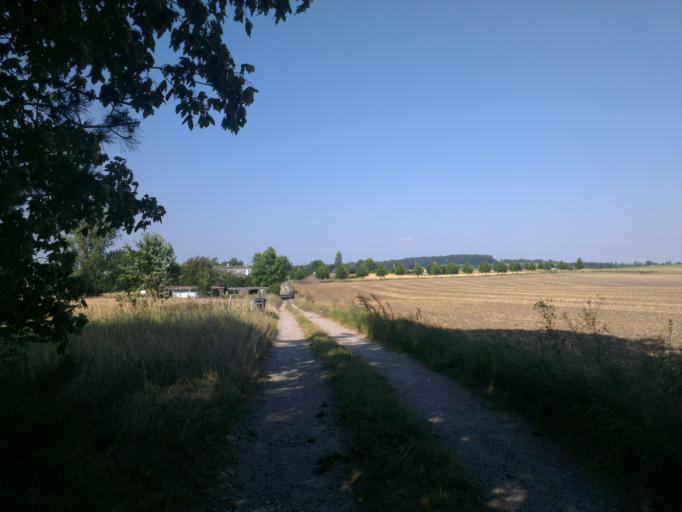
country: DK
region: Capital Region
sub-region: Frederikssund Kommune
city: Skibby
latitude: 55.7645
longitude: 11.9460
